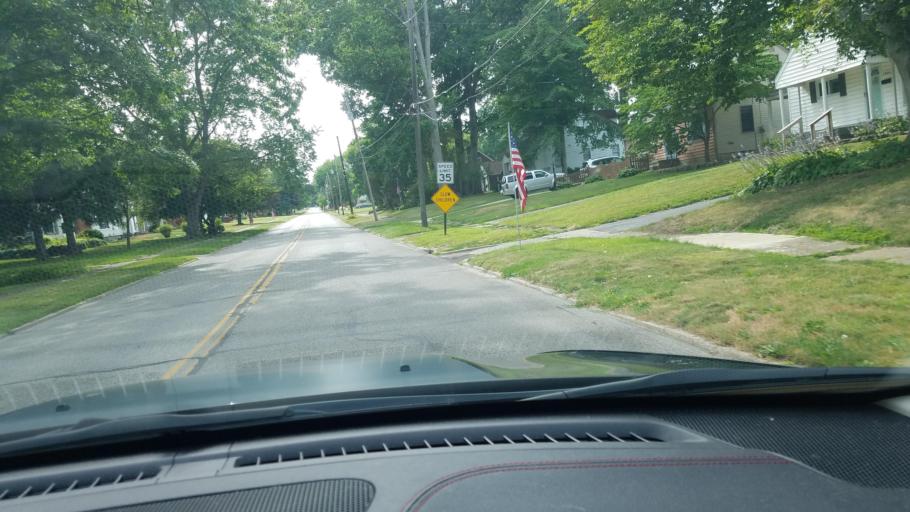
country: US
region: Ohio
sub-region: Mahoning County
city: Struthers
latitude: 41.0382
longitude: -80.6058
